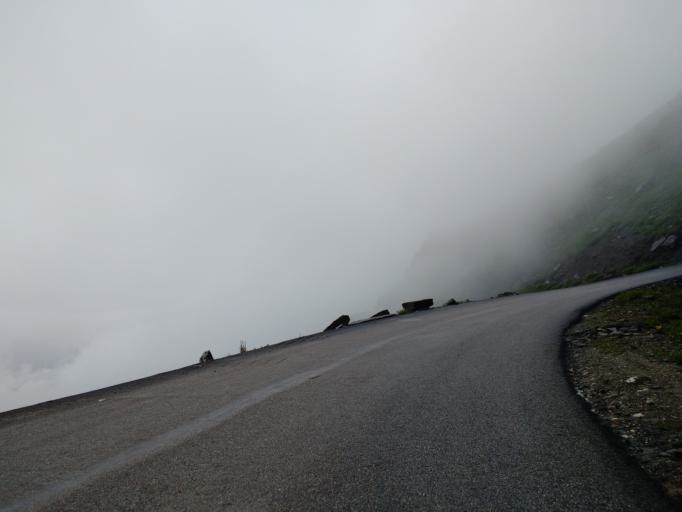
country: IN
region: Himachal Pradesh
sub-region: Kulu
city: Manali
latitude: 32.3560
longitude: 77.2229
